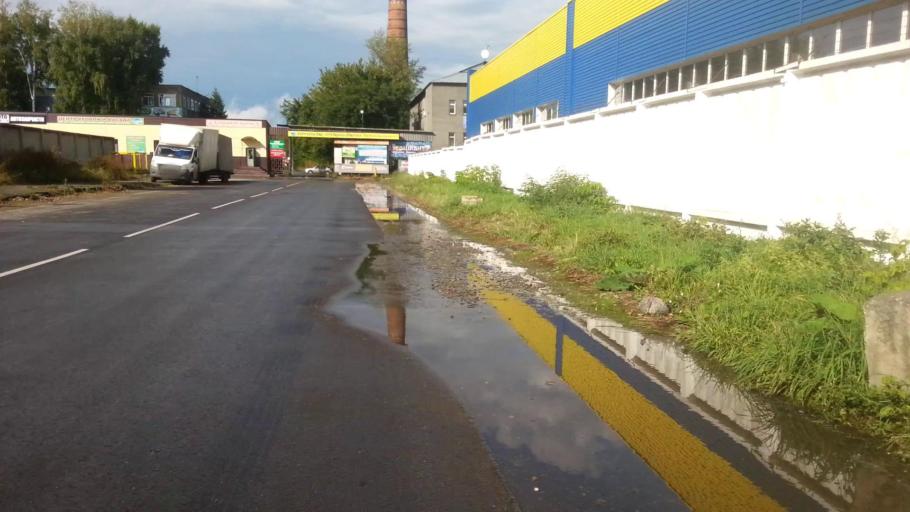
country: RU
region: Altai Krai
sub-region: Gorod Barnaulskiy
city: Barnaul
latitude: 53.3437
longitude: 83.7230
